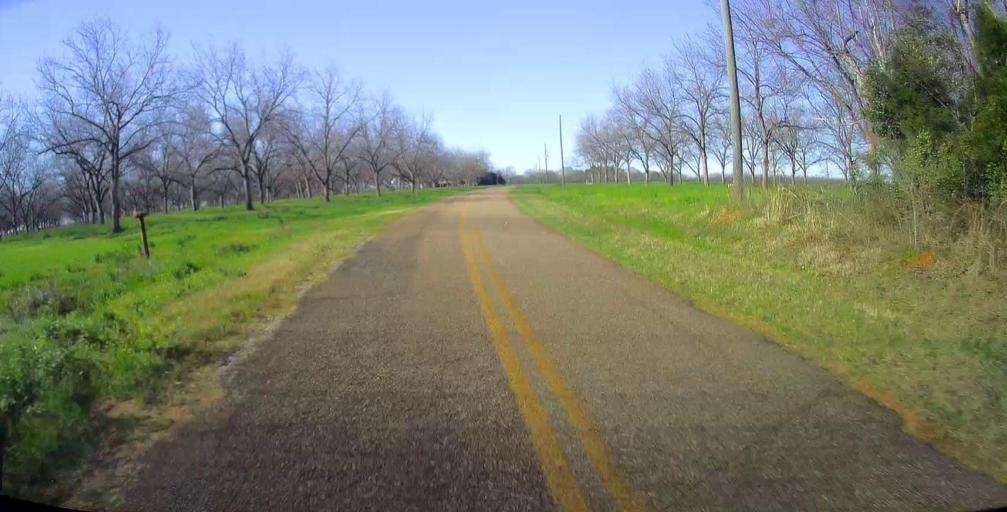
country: US
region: Georgia
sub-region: Macon County
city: Marshallville
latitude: 32.4936
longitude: -83.9524
